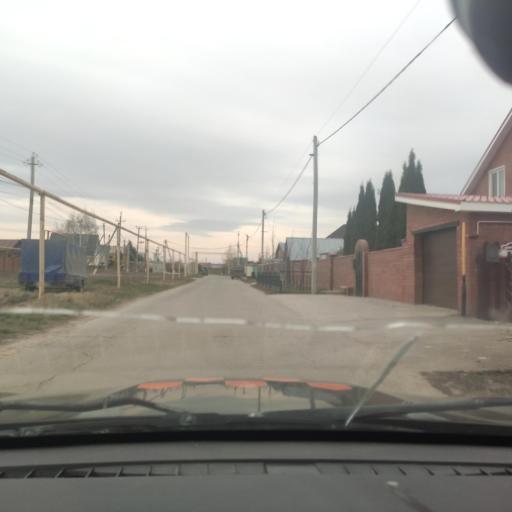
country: RU
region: Samara
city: Podstepki
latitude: 53.5135
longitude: 49.1357
